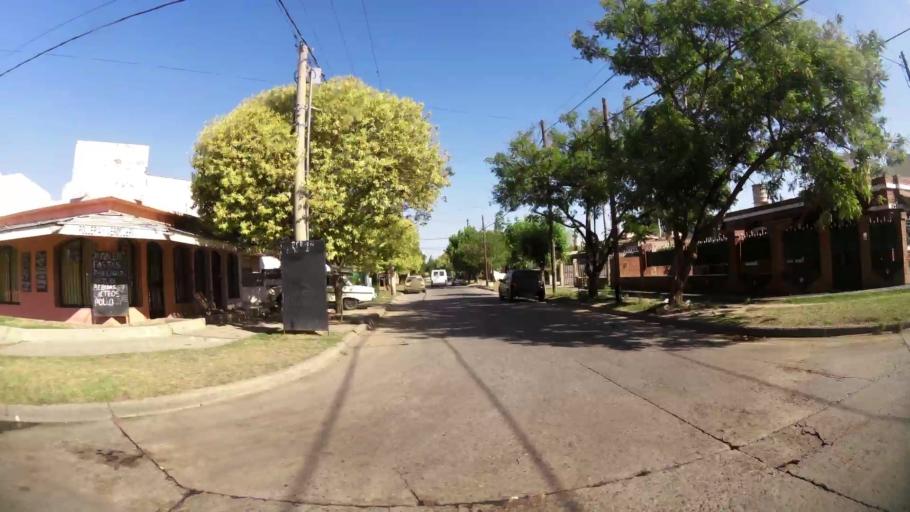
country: AR
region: Cordoba
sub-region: Departamento de Capital
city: Cordoba
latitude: -31.3632
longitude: -64.1887
